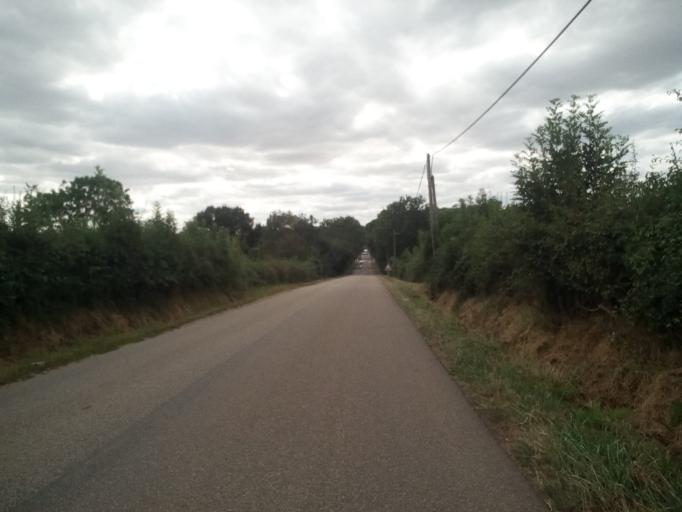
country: FR
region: Lower Normandy
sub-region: Departement du Calvados
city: Troarn
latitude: 49.1662
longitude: -0.1456
